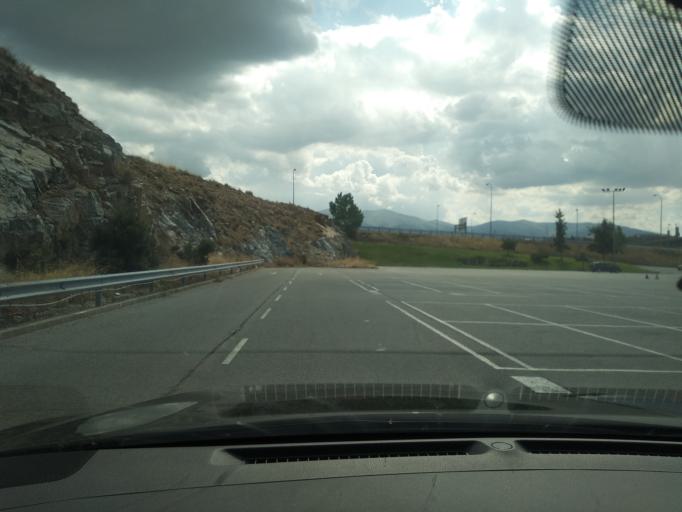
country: ES
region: Castille and Leon
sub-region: Provincia de Segovia
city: Segovia
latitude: 40.9209
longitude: -4.1112
